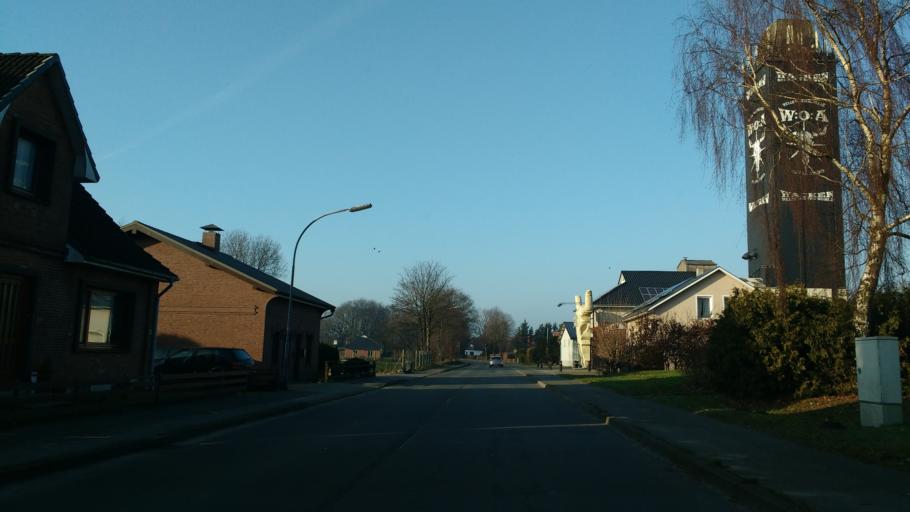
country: DE
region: Schleswig-Holstein
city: Wacken
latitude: 54.0255
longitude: 9.3662
